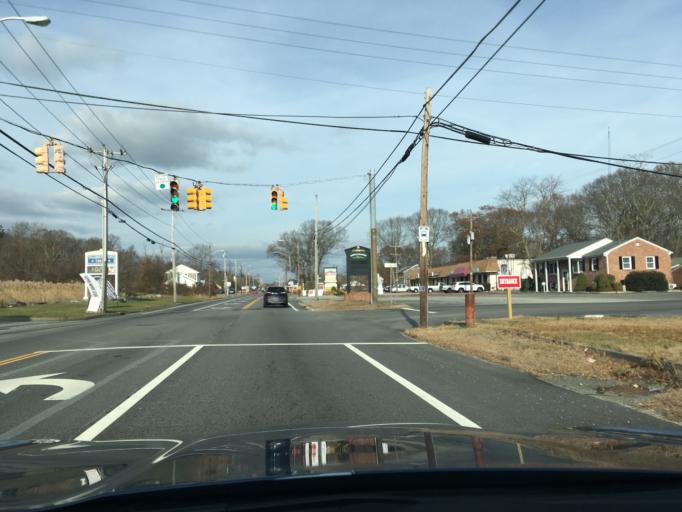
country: US
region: Rhode Island
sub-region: Washington County
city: North Kingstown
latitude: 41.5899
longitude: -71.4575
